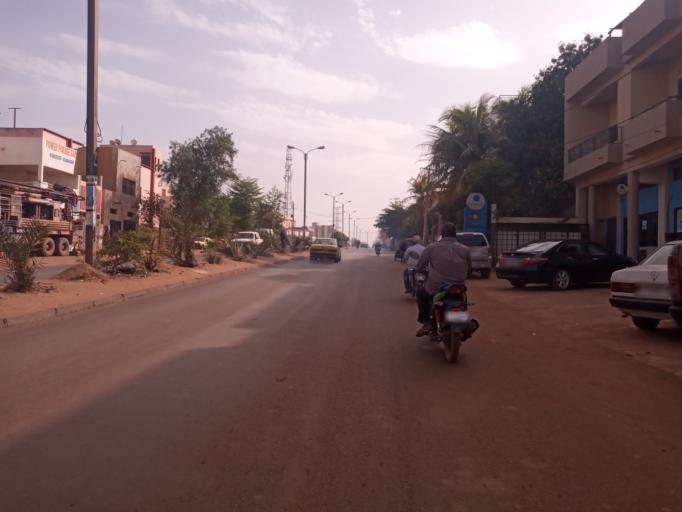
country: ML
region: Bamako
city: Bamako
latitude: 12.5797
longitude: -7.9473
